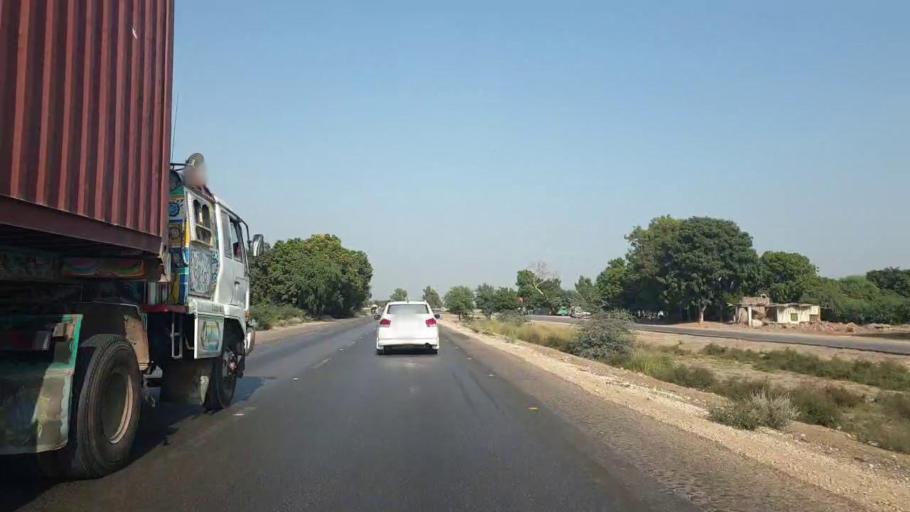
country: PK
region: Sindh
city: Hyderabad
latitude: 25.4882
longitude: 68.4198
